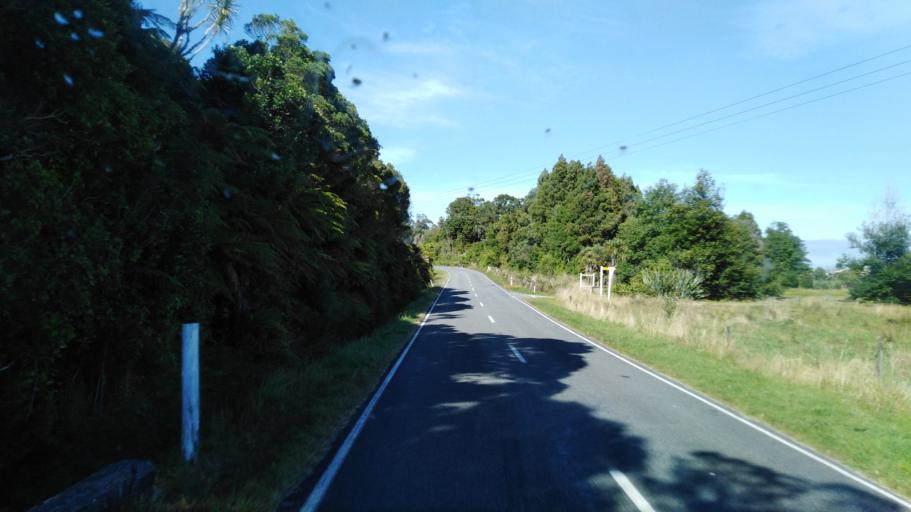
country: NZ
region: West Coast
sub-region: Buller District
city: Westport
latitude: -41.2688
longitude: 172.1108
